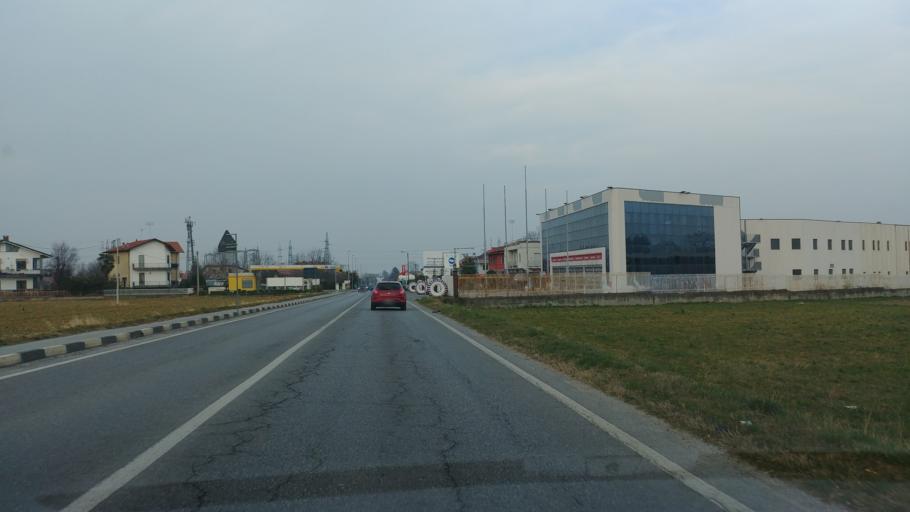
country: IT
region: Piedmont
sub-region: Provincia di Cuneo
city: Borgo San Dalmazzo
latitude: 44.3548
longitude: 7.5123
